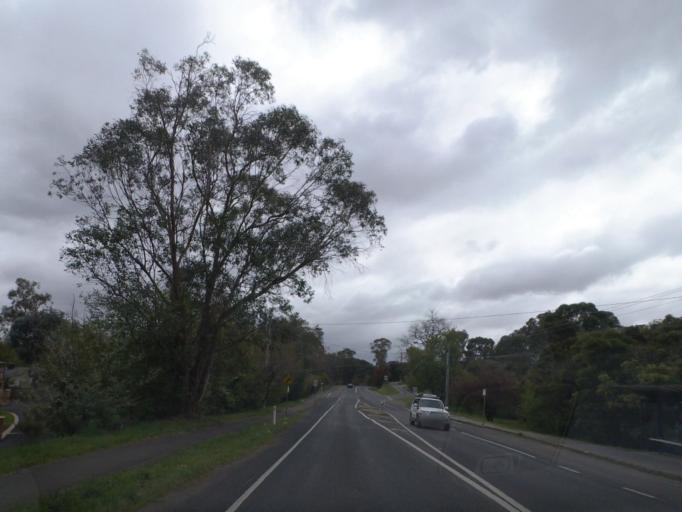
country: AU
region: Victoria
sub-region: Nillumbik
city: North Warrandyte
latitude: -37.7442
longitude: 145.2107
